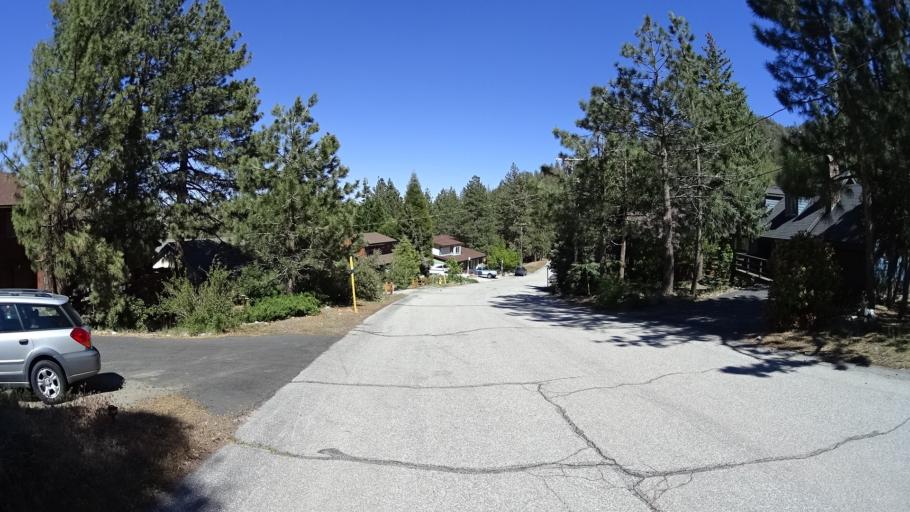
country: US
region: California
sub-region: San Bernardino County
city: Wrightwood
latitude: 34.3614
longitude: -117.6552
